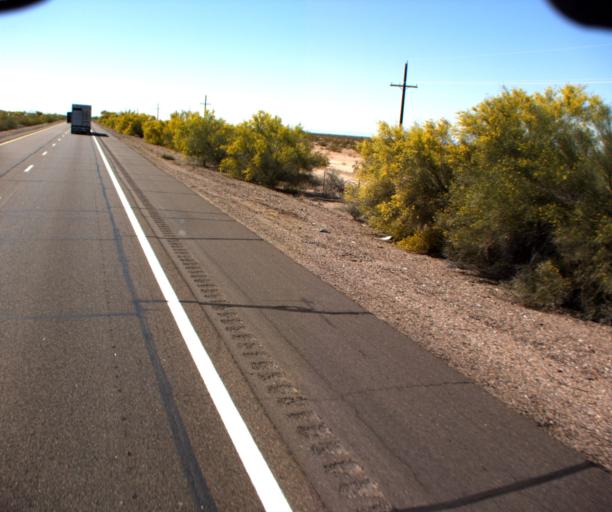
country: US
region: Arizona
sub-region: Maricopa County
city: Gila Bend
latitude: 32.8429
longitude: -113.3025
